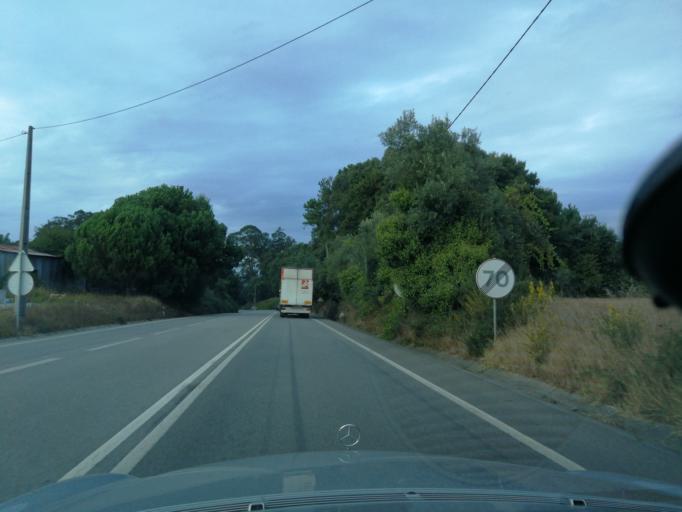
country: PT
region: Aveiro
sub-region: Agueda
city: Valongo
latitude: 40.6231
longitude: -8.4614
